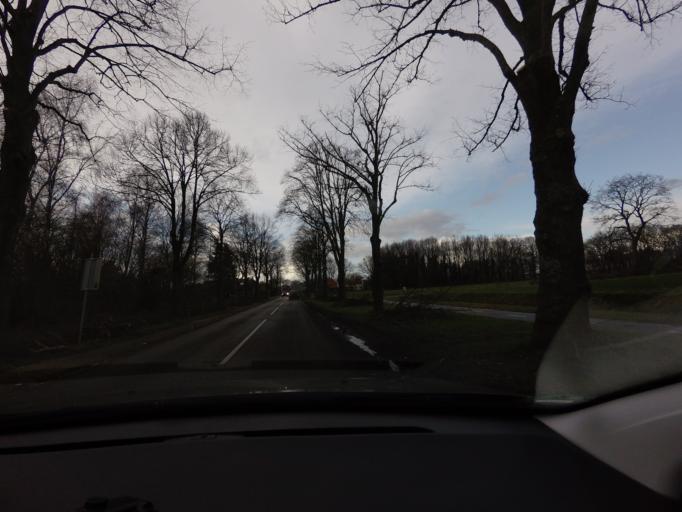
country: NL
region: Drenthe
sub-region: Gemeente Assen
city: Assen
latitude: 52.8444
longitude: 6.6235
